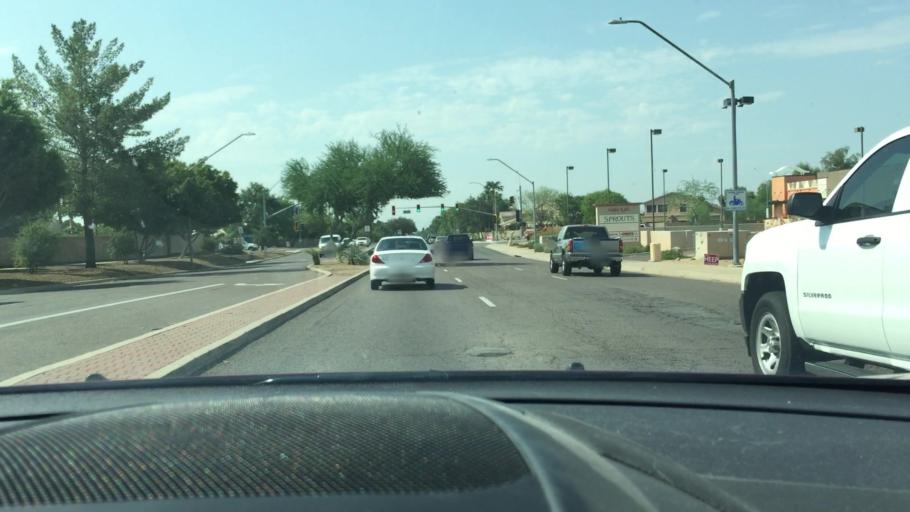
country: US
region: Arizona
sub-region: Maricopa County
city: Peoria
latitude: 33.6830
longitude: -112.2032
